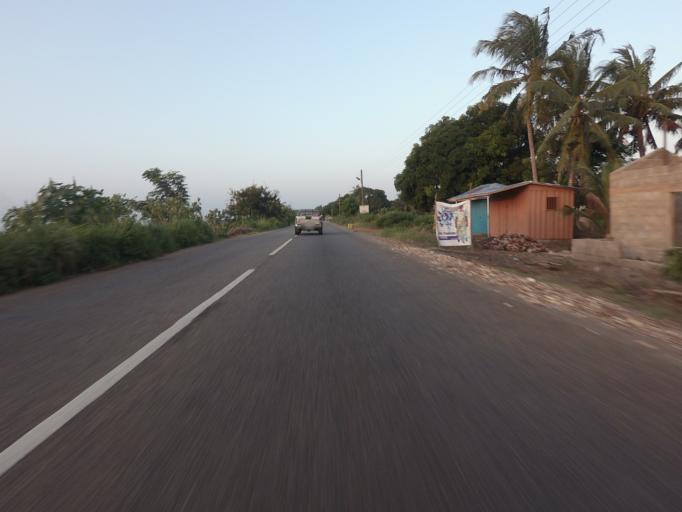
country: GH
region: Volta
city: Anloga
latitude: 5.8119
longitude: 0.9348
